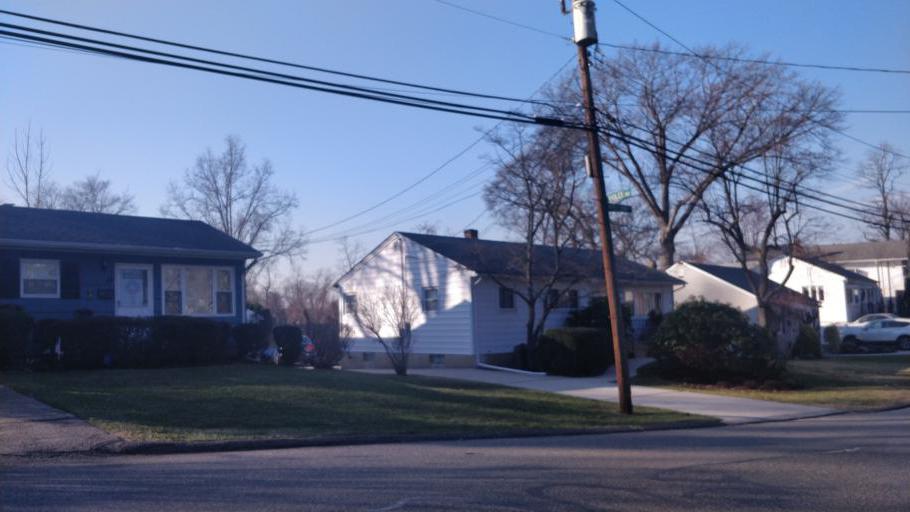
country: US
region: New York
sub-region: Nassau County
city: Bayville
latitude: 40.9074
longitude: -73.5776
